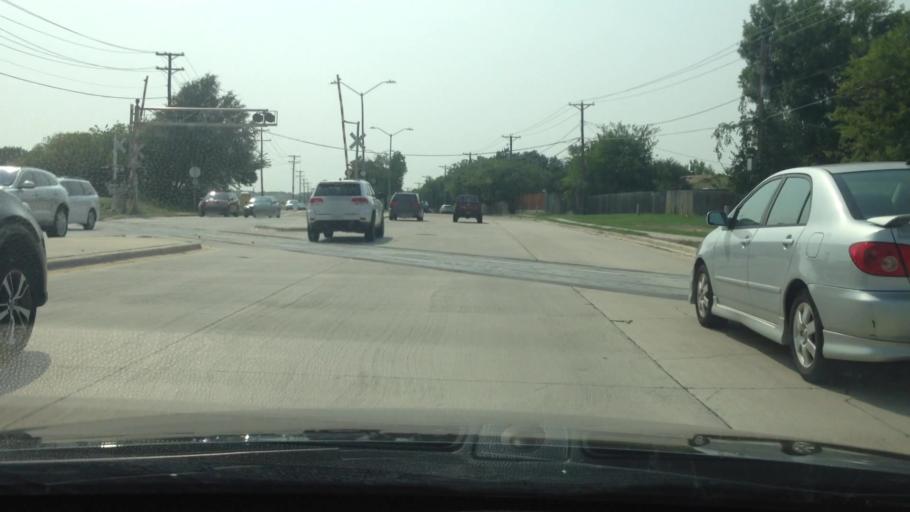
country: US
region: Texas
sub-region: Tarrant County
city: North Richland Hills
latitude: 32.8602
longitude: -97.2210
